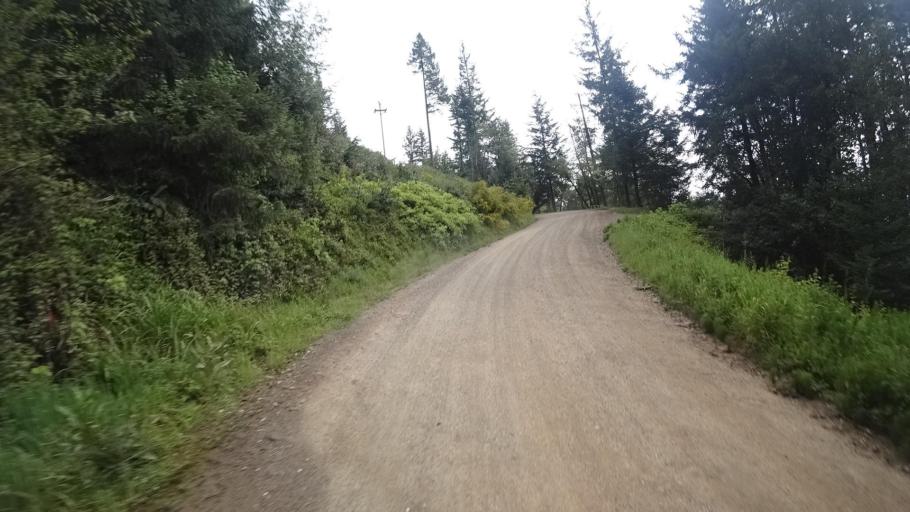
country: US
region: California
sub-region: Humboldt County
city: Redway
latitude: 40.2498
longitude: -123.7656
